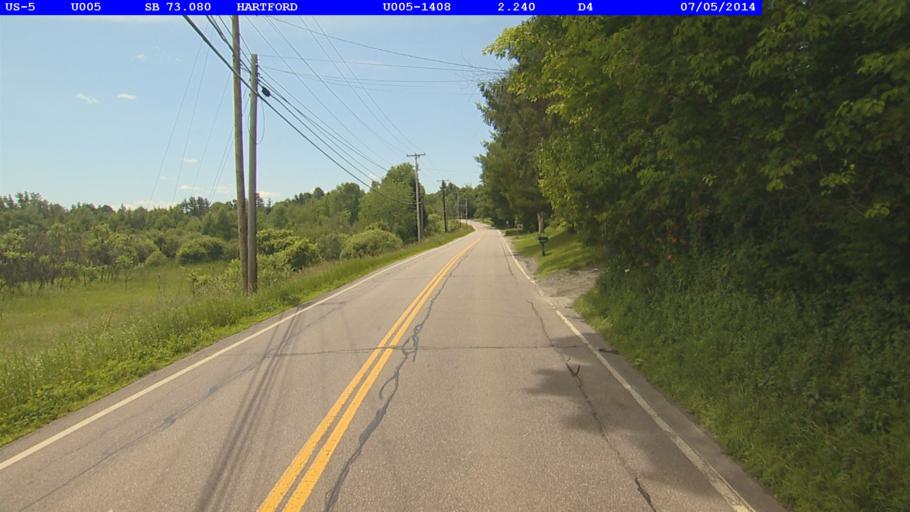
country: US
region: Vermont
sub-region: Windsor County
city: White River Junction
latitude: 43.6418
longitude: -72.3469
